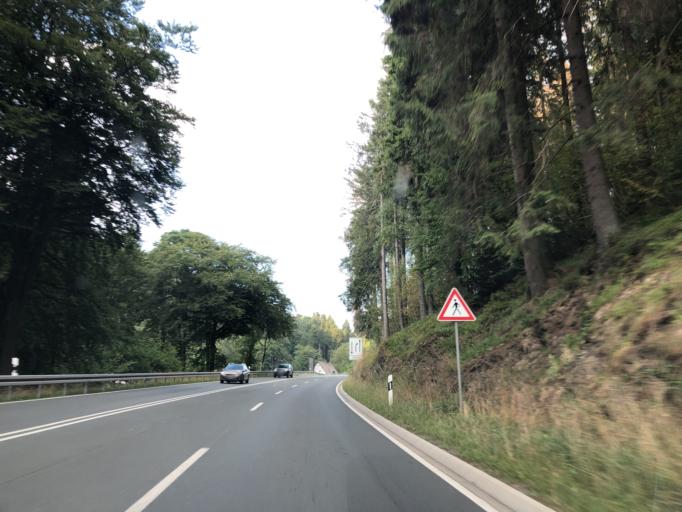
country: DE
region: North Rhine-Westphalia
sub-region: Regierungsbezirk Arnsberg
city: Winterberg
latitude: 51.1891
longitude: 8.5219
